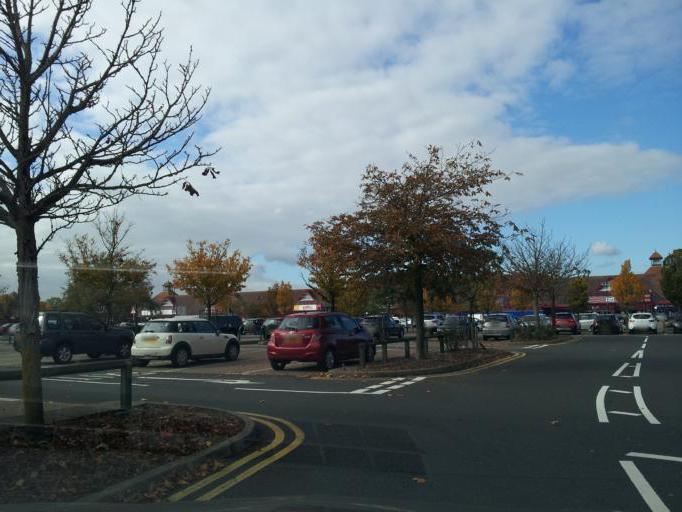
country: GB
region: England
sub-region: Milton Keynes
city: Shenley Church End
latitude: 52.0048
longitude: -0.7921
